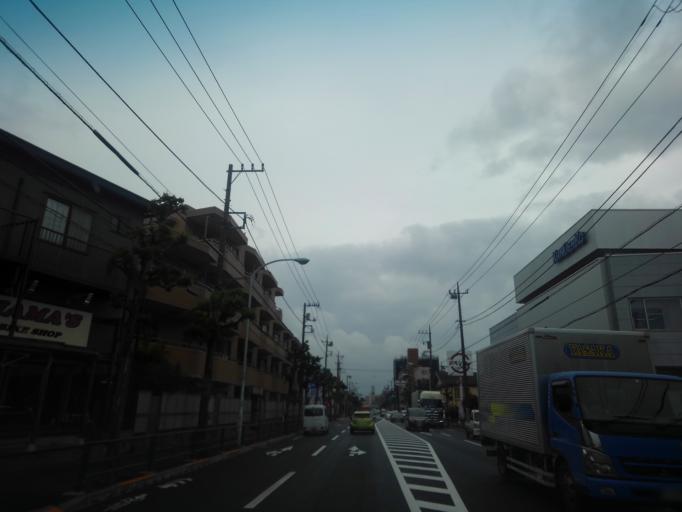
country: JP
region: Tokyo
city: Tanashicho
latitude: 35.7343
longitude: 139.5294
